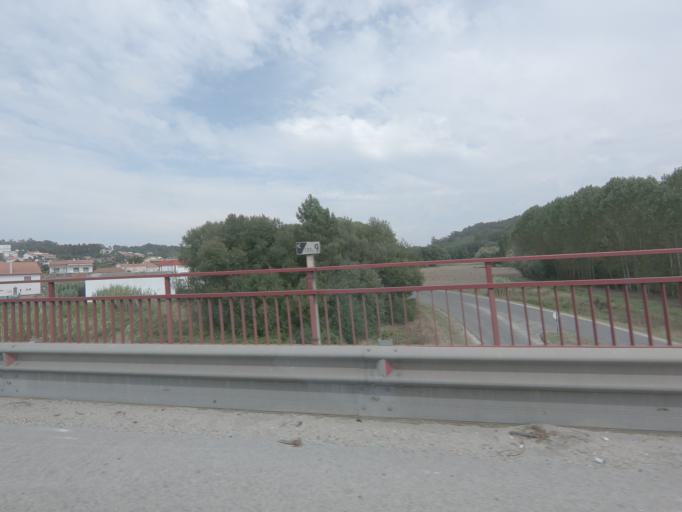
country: PT
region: Leiria
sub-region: Leiria
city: Caranguejeira
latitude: 39.8061
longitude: -8.7419
